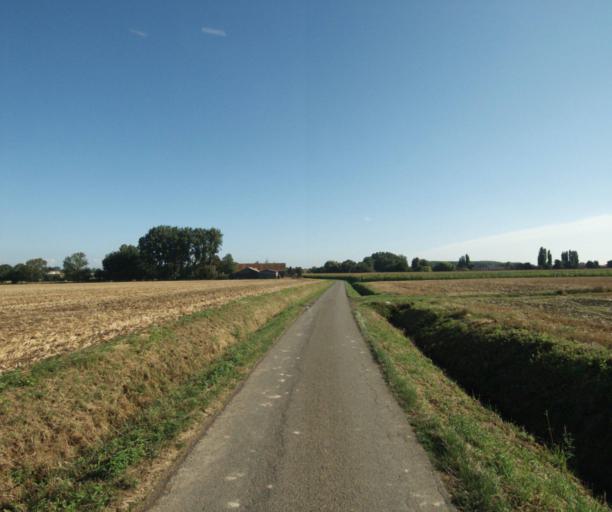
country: FR
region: Nord-Pas-de-Calais
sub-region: Departement du Nord
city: Willems
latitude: 50.6477
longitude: 3.2458
